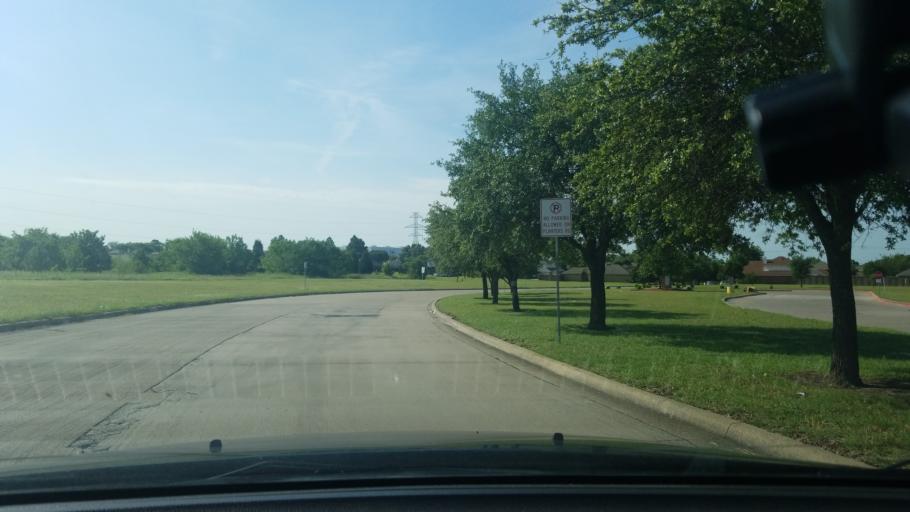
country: US
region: Texas
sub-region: Dallas County
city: Sunnyvale
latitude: 32.7818
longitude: -96.5748
